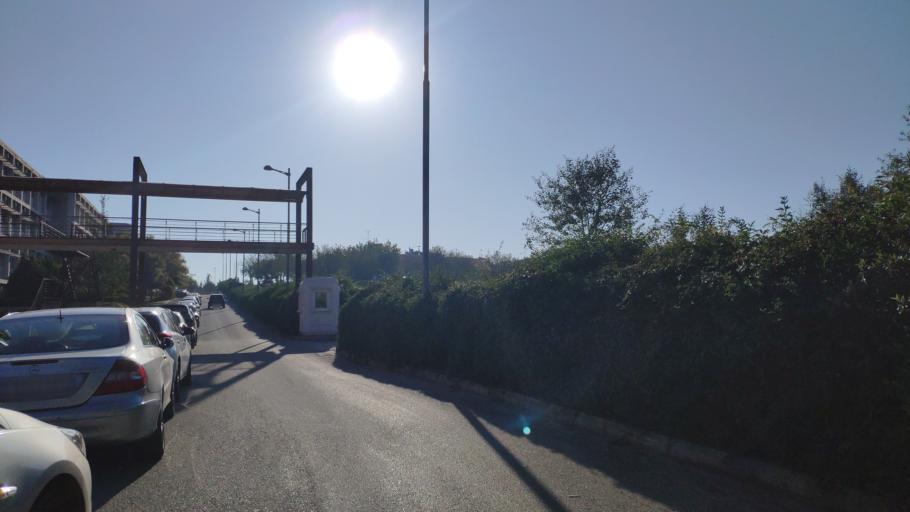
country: GR
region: Thessaly
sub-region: Nomos Larisis
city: Terpsithea
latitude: 39.6143
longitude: 22.3868
